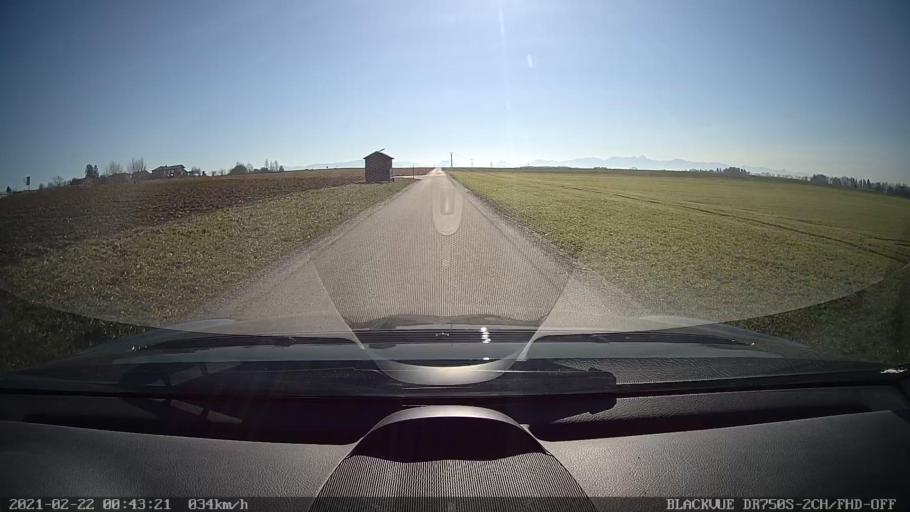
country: DE
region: Bavaria
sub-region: Upper Bavaria
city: Griesstatt
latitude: 47.9920
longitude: 12.1719
